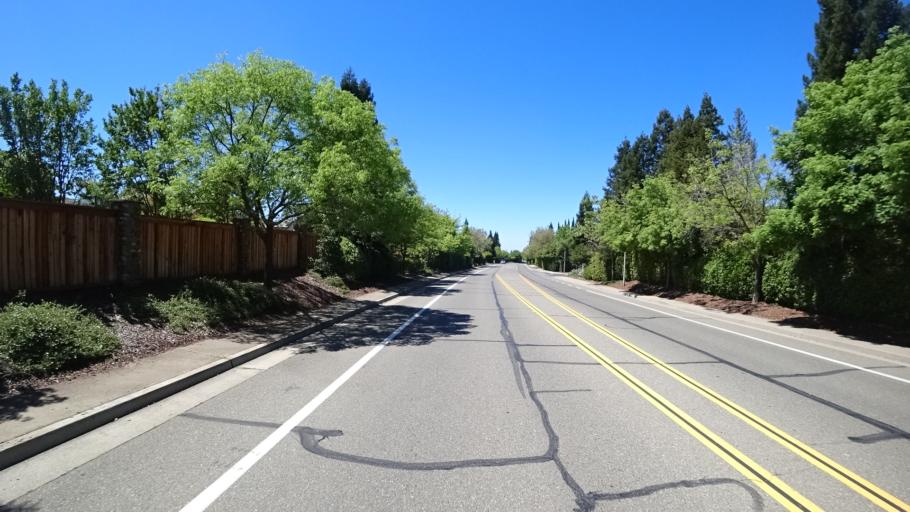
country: US
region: California
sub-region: Placer County
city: Rocklin
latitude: 38.8071
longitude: -121.2512
